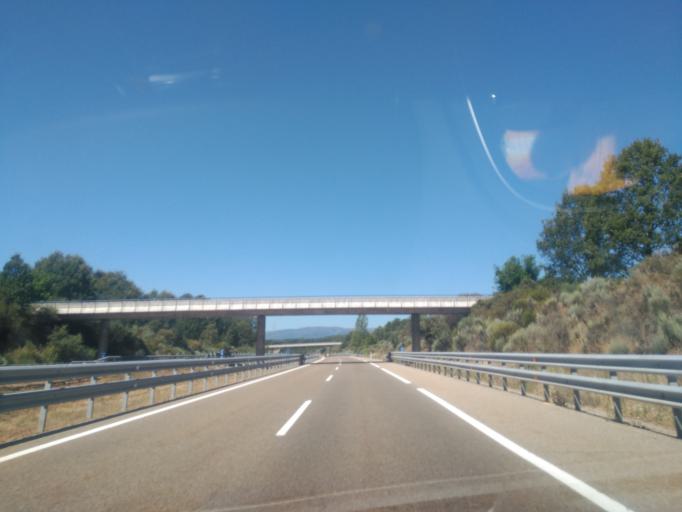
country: ES
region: Castille and Leon
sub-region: Provincia de Zamora
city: Asturianos
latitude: 42.0454
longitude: -6.4952
